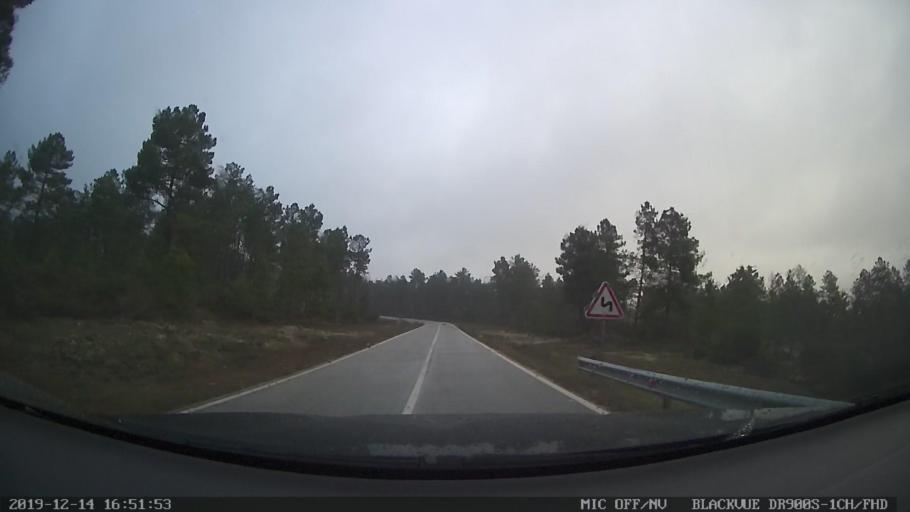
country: PT
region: Vila Real
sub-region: Murca
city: Murca
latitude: 41.4261
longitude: -7.5042
